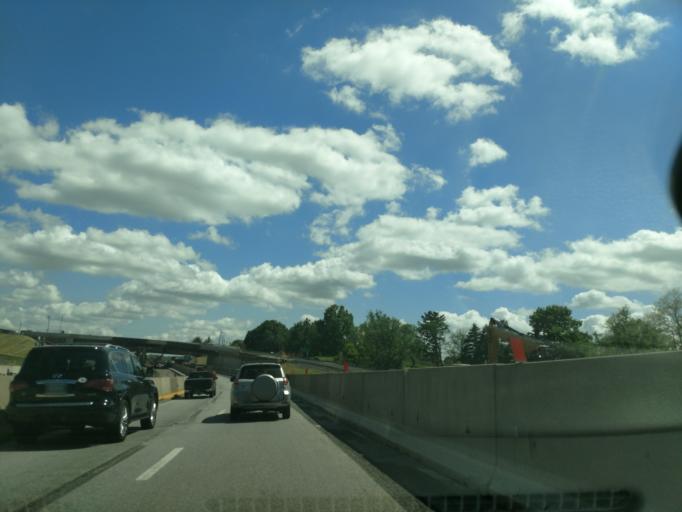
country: US
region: Pennsylvania
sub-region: Montgomery County
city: Audubon
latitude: 40.1038
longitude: -75.4199
